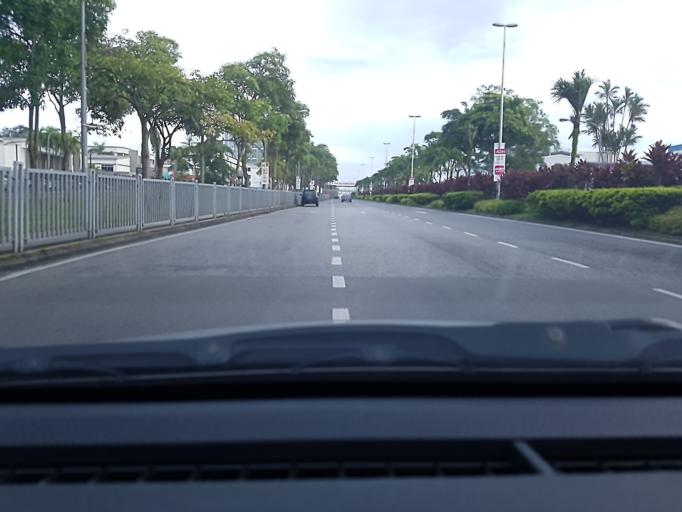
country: MY
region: Sarawak
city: Kuching
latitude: 1.5329
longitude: 110.3580
